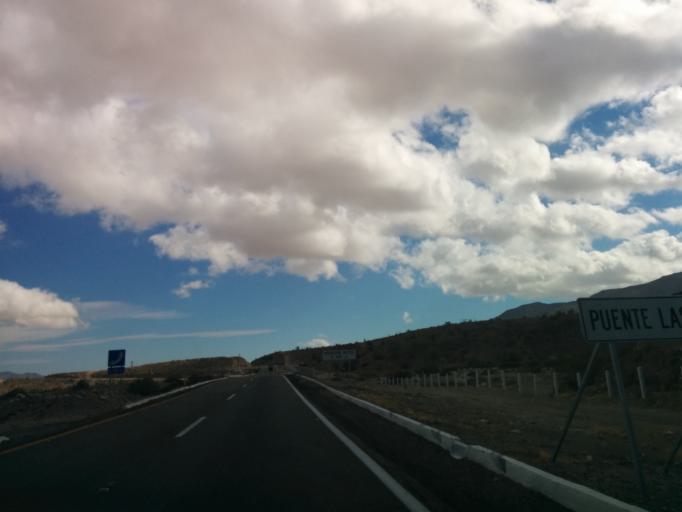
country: MX
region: Baja California
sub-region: Tecate
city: Cereso del Hongo
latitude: 32.5658
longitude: -115.9539
